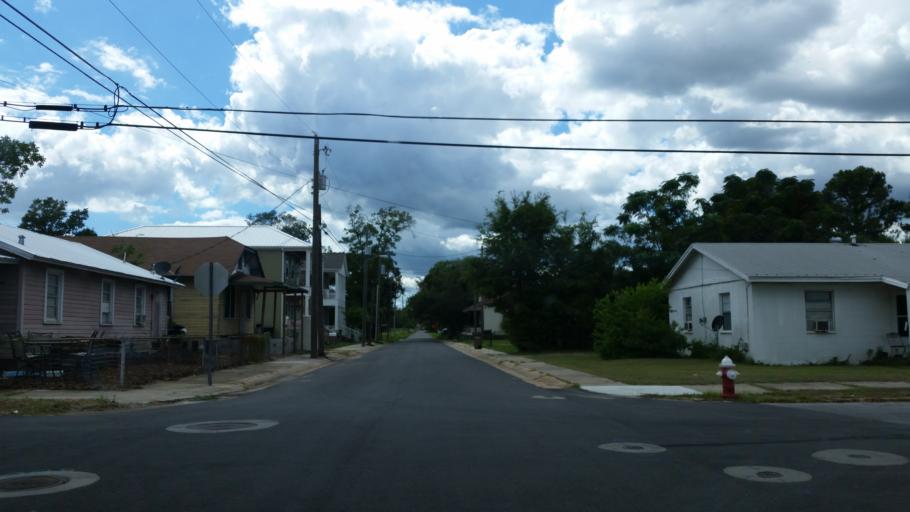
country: US
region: Florida
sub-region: Escambia County
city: Pensacola
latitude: 30.4092
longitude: -87.2212
